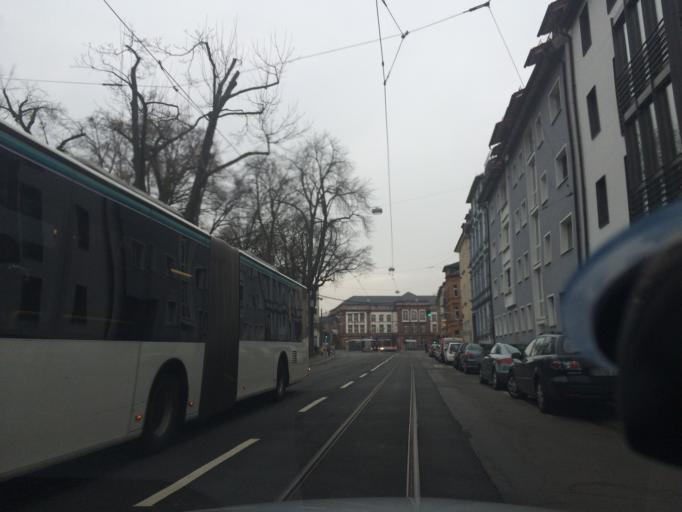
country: DE
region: Hesse
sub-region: Regierungsbezirk Darmstadt
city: Darmstadt
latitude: 49.8777
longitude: 8.6504
